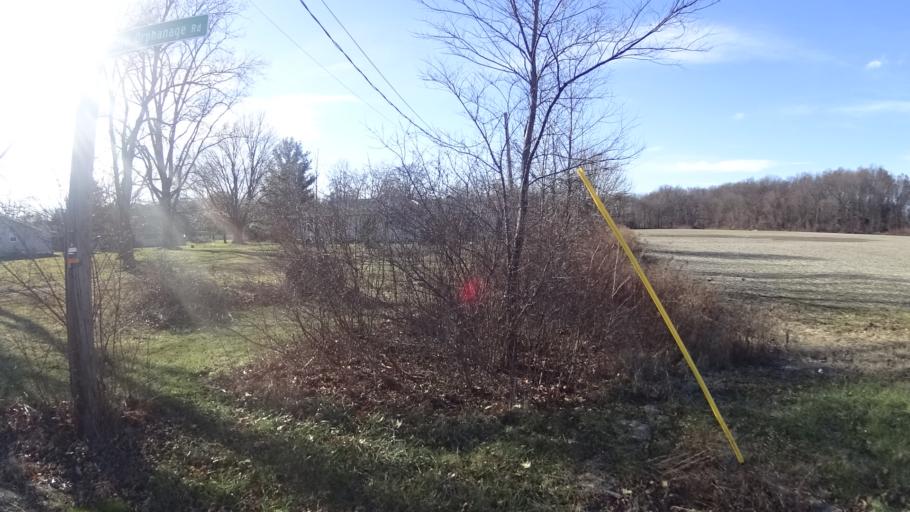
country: US
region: Ohio
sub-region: Lorain County
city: Vermilion-on-the-Lake
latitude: 41.3687
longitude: -82.3288
